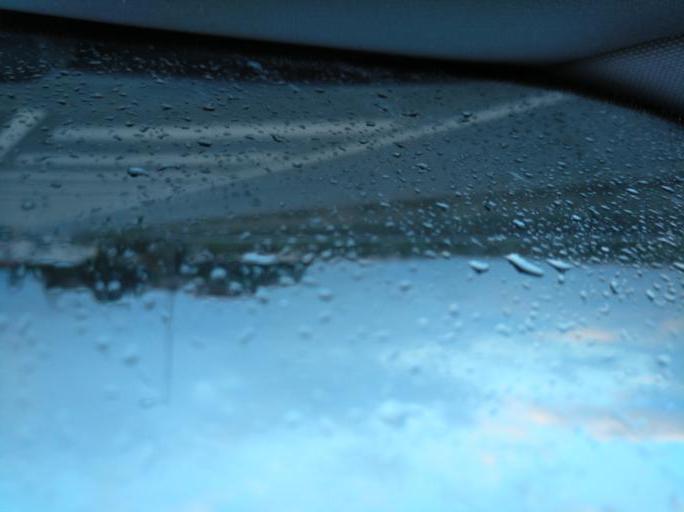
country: PT
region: Faro
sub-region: Castro Marim
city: Castro Marim
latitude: 37.2220
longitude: -7.4446
